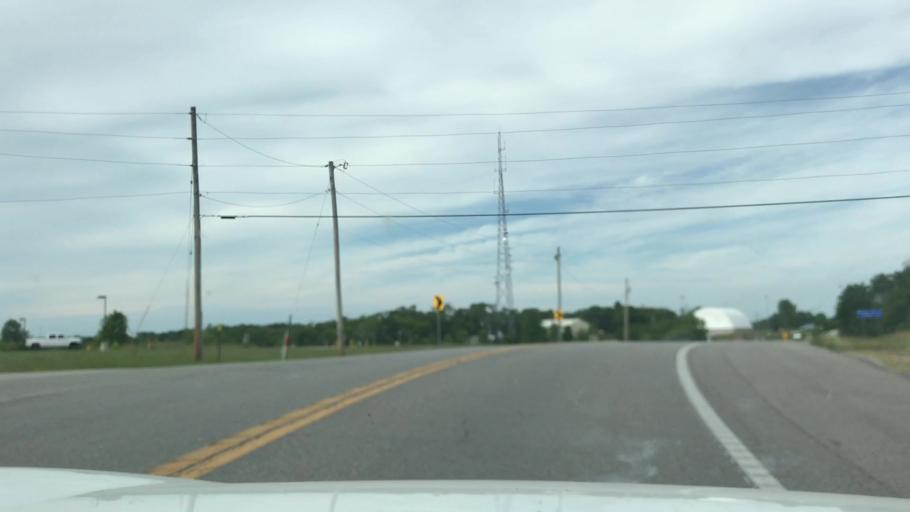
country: US
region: Missouri
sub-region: Saint Charles County
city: Weldon Spring
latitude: 38.6949
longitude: -90.7241
